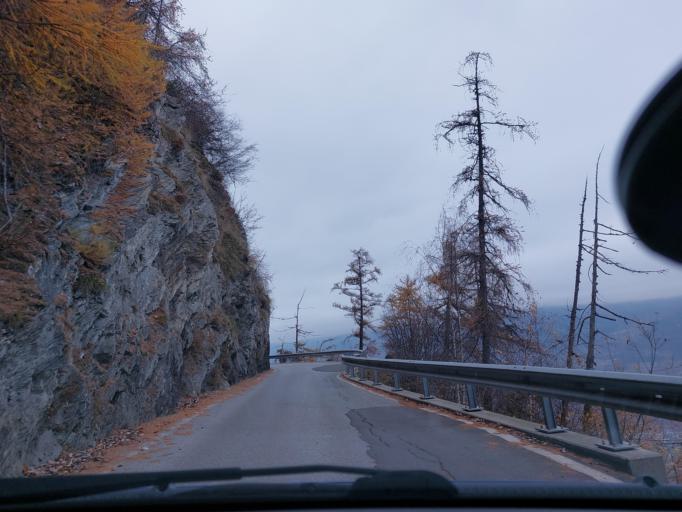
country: CH
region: Valais
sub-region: Martigny District
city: Riddes
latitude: 46.1702
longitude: 7.2437
